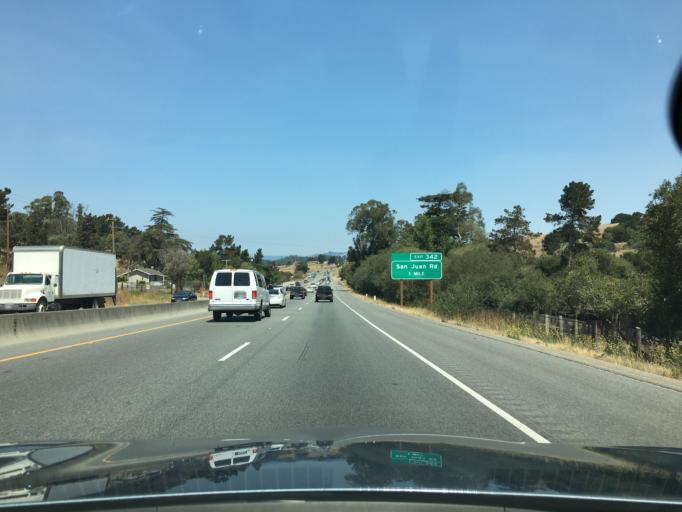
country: US
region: California
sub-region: San Benito County
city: Aromas
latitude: 36.8417
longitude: -121.6329
